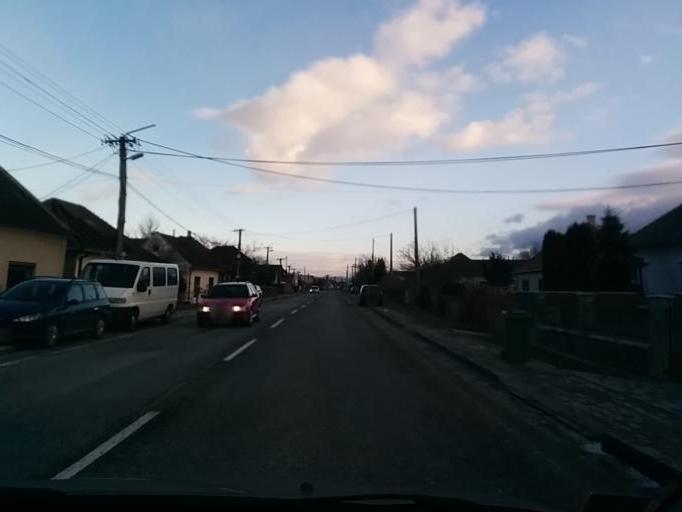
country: SK
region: Nitriansky
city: Cachtice
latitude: 48.6856
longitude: 17.8472
